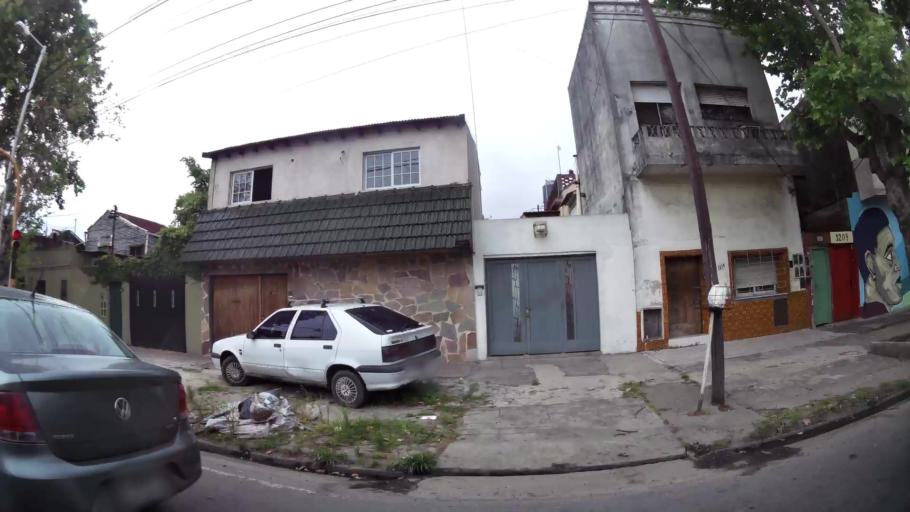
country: AR
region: Buenos Aires
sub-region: Partido de Avellaneda
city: Avellaneda
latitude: -34.6619
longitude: -58.3563
